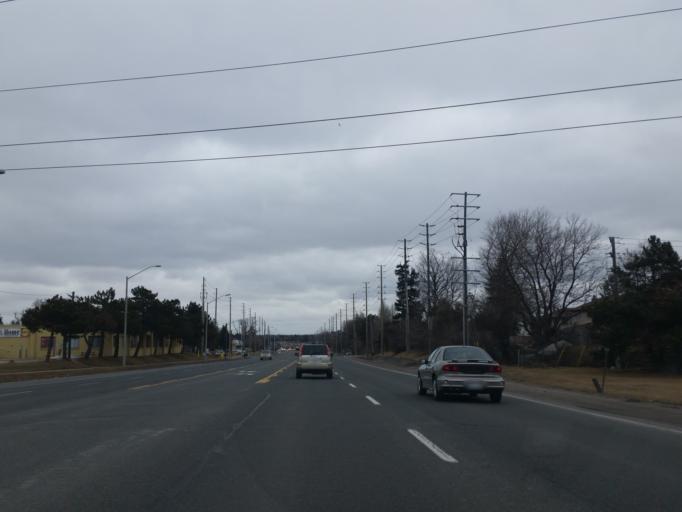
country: CA
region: Ontario
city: Ajax
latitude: 43.8445
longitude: -79.0790
